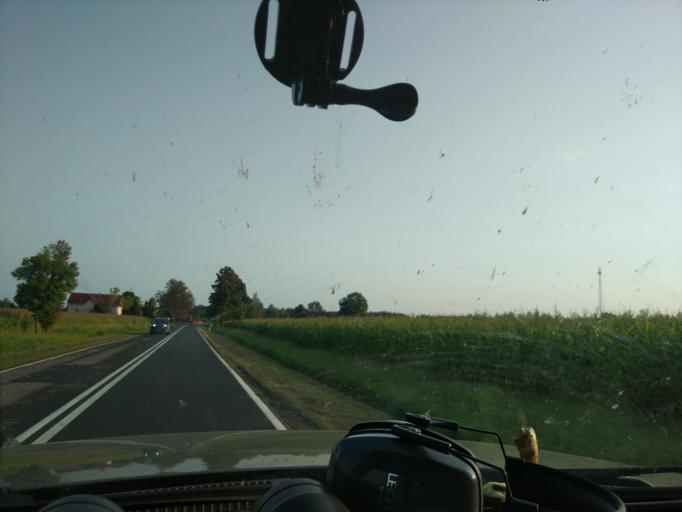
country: PL
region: Warmian-Masurian Voivodeship
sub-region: Powiat szczycienski
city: Wielbark
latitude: 53.3511
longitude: 20.9003
